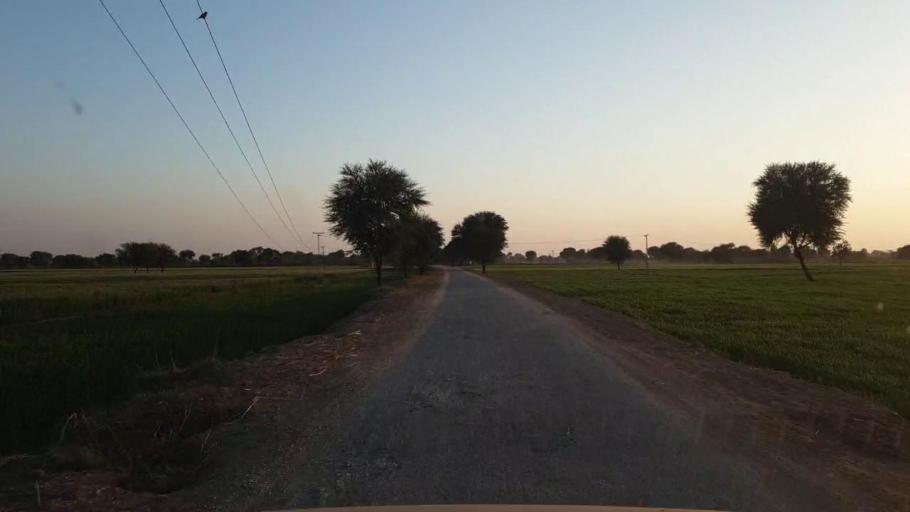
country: PK
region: Sindh
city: Tando Jam
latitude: 25.3070
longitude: 68.6385
